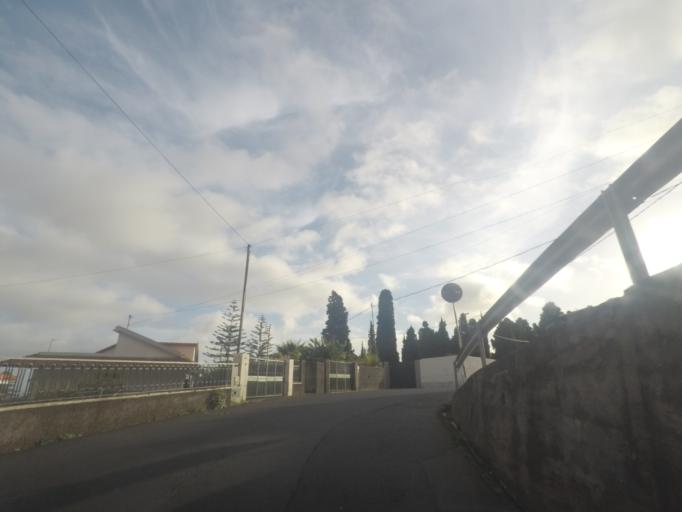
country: PT
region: Madeira
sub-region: Funchal
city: Nossa Senhora do Monte
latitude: 32.6692
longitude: -16.9396
